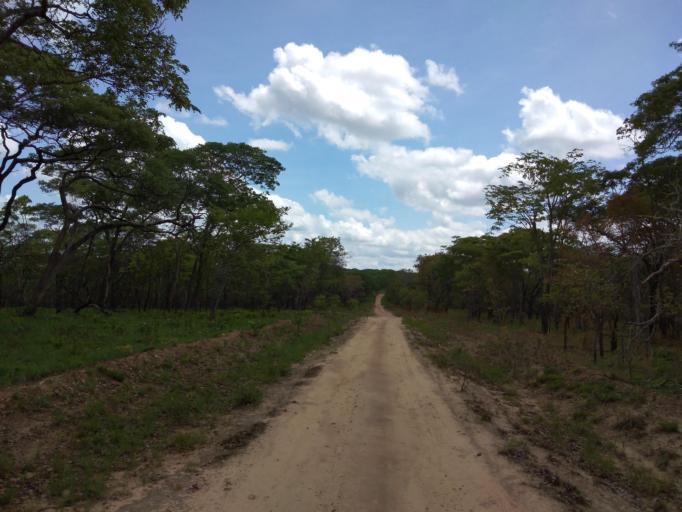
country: ZM
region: Central
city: Mkushi
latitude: -14.0496
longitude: 29.9638
